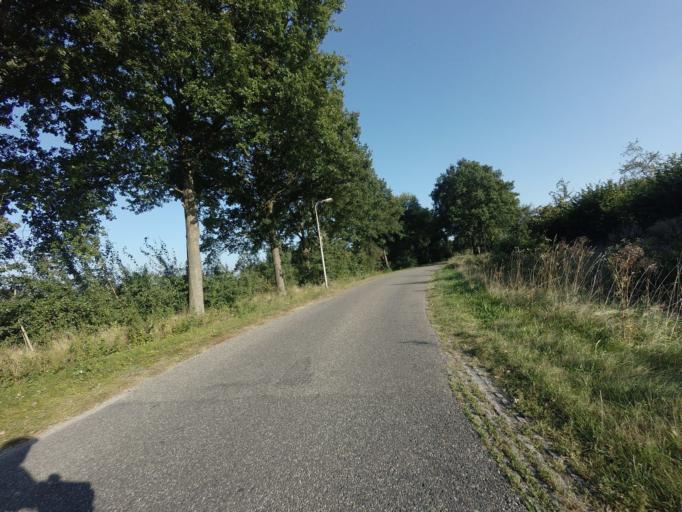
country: NL
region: Overijssel
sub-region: Gemeente Hardenberg
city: Hardenberg
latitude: 52.5524
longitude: 6.6528
